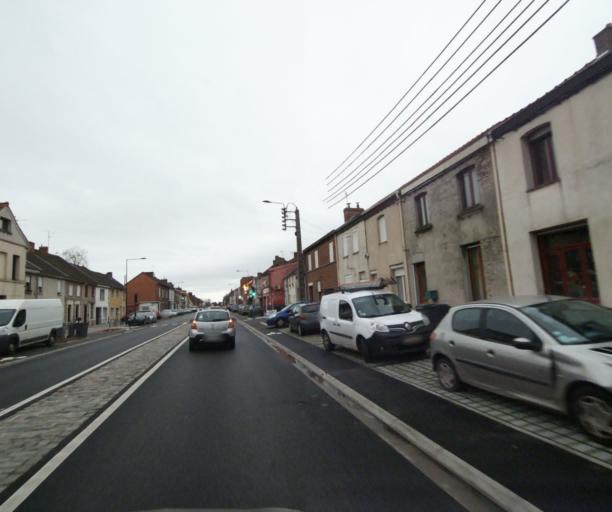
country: FR
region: Nord-Pas-de-Calais
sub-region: Departement du Nord
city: La Sentinelle
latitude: 50.3504
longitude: 3.4907
